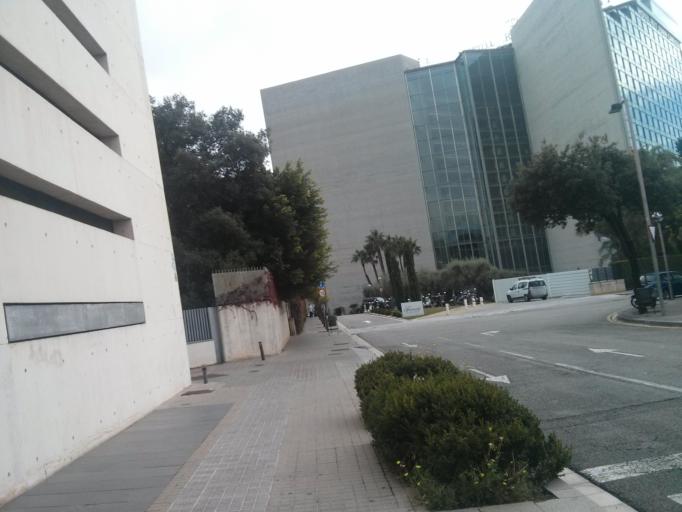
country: ES
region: Catalonia
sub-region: Provincia de Barcelona
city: les Corts
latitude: 41.3824
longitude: 2.1092
